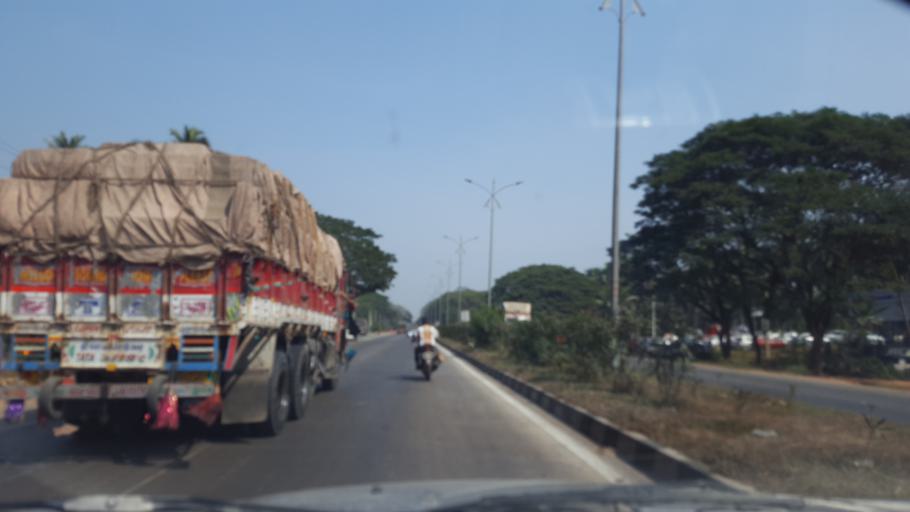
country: IN
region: Andhra Pradesh
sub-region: Vishakhapatnam
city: Anakapalle
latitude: 17.6752
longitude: 83.0068
